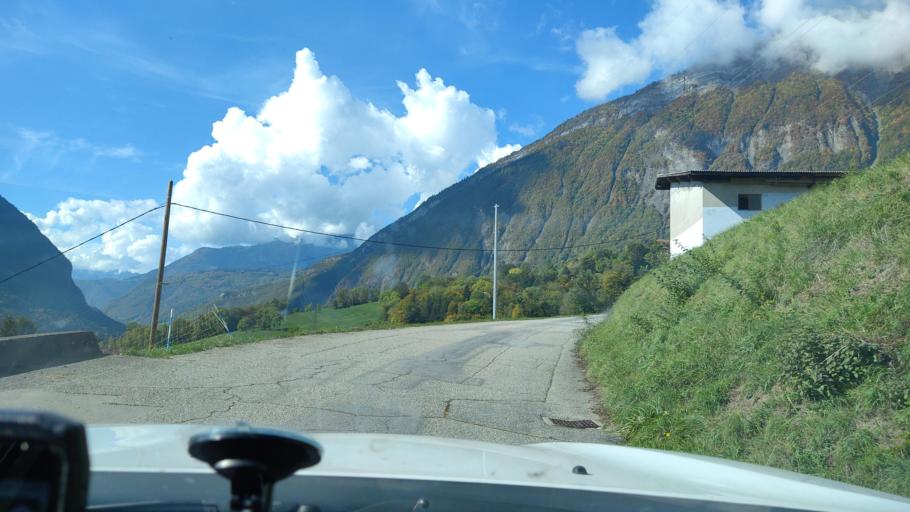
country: FR
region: Rhone-Alpes
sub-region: Departement de la Savoie
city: Ugine
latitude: 45.7623
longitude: 6.4160
